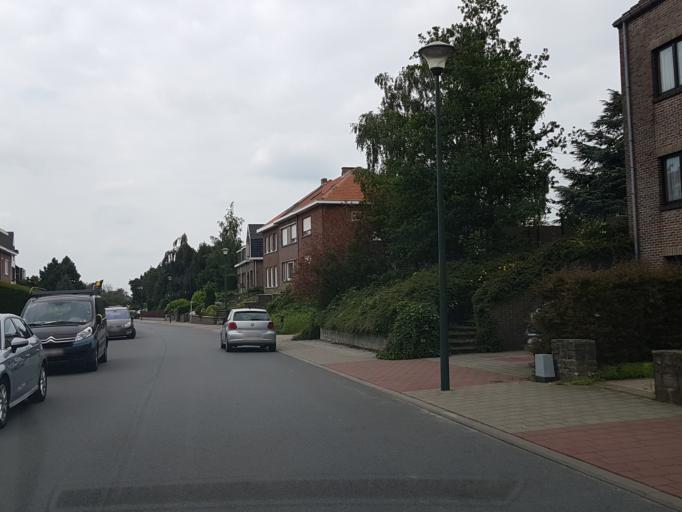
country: BE
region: Flanders
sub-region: Provincie Vlaams-Brabant
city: Kraainem
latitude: 50.8687
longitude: 4.4417
